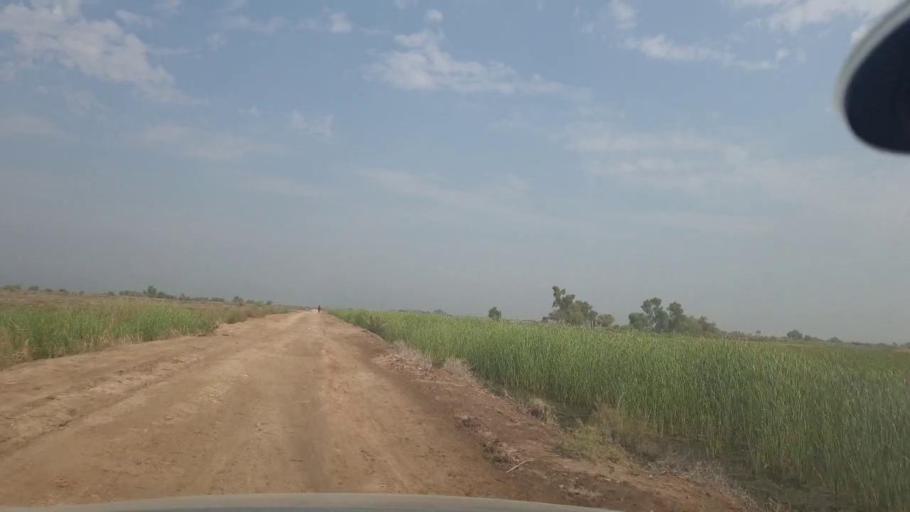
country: PK
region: Balochistan
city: Mehrabpur
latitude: 28.0280
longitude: 68.1323
